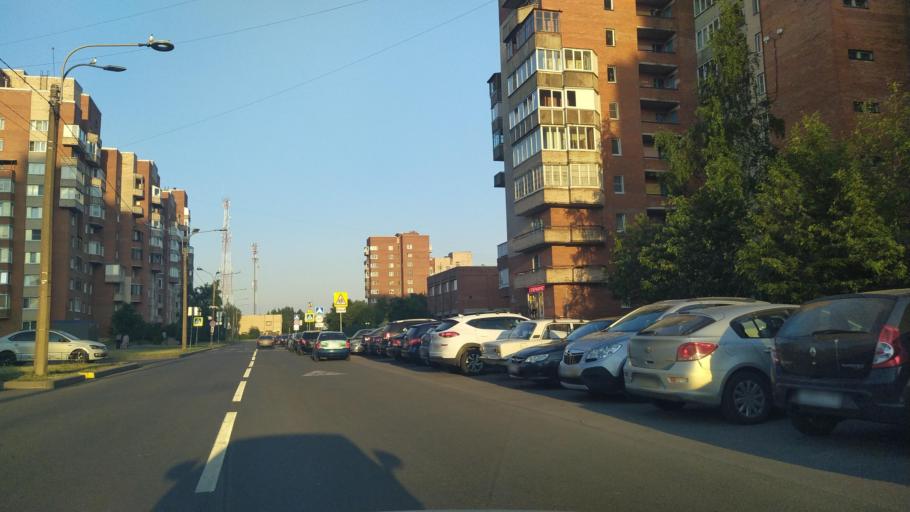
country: RU
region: St.-Petersburg
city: Kronshtadt
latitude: 60.0098
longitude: 29.7216
